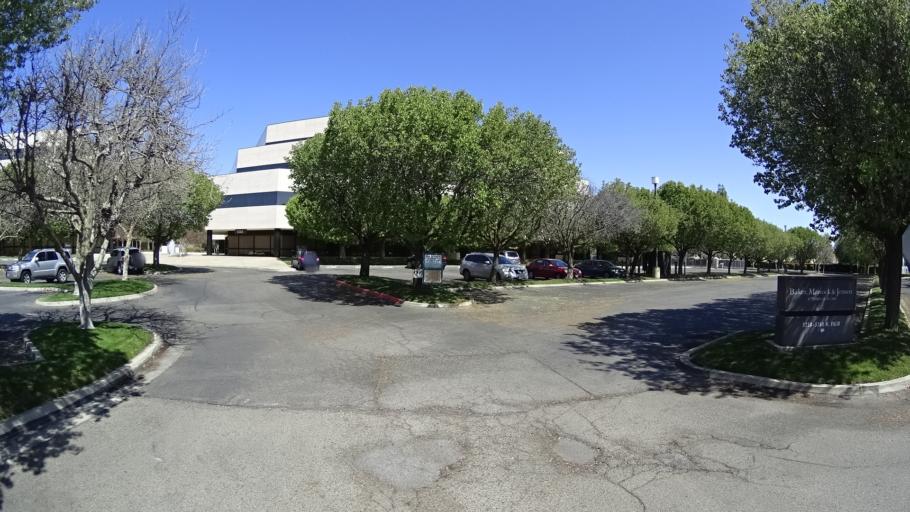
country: US
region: California
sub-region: Fresno County
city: Fresno
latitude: 36.8120
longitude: -119.8060
